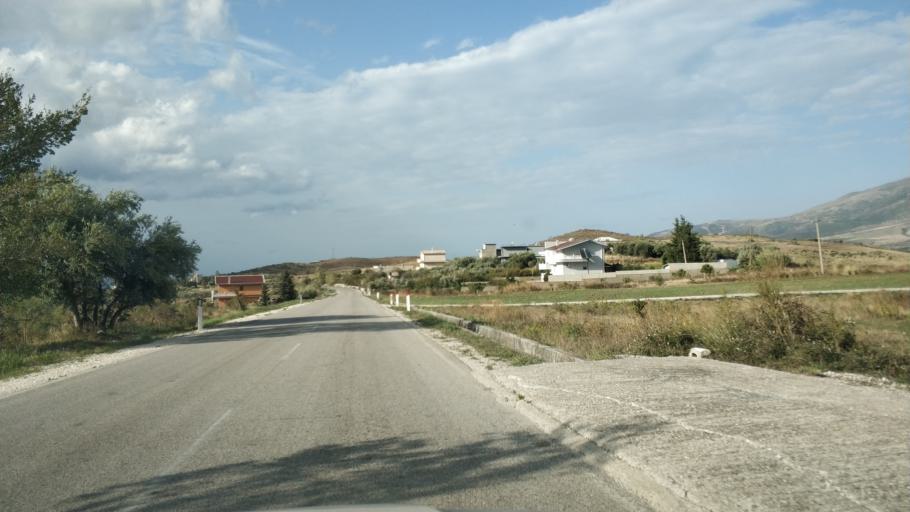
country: AL
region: Vlore
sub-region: Rrethi i Vlores
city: Orikum
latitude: 40.3071
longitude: 19.4817
